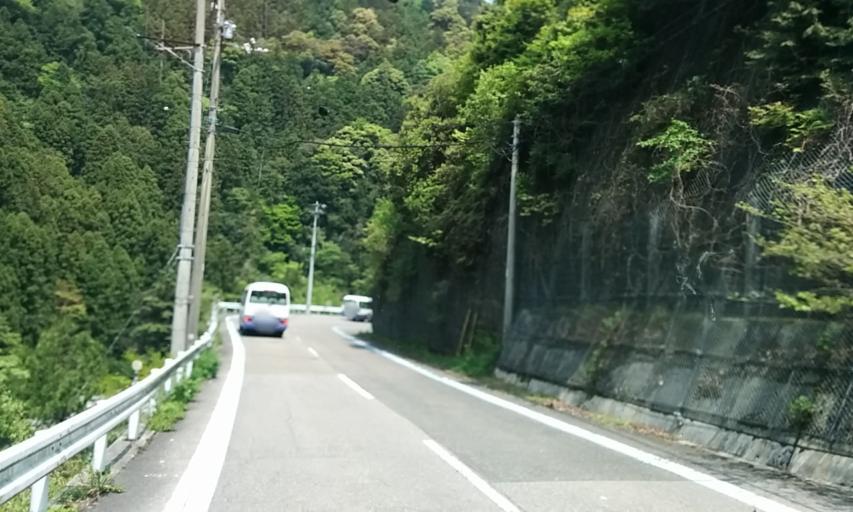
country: JP
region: Ehime
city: Niihama
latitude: 33.8826
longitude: 133.3007
